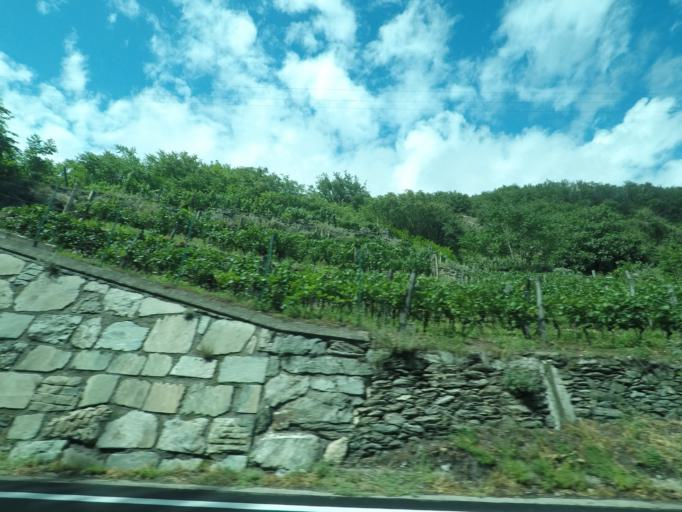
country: IT
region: Aosta Valley
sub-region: Valle d'Aosta
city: Saint Marcel
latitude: 45.7401
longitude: 7.4493
